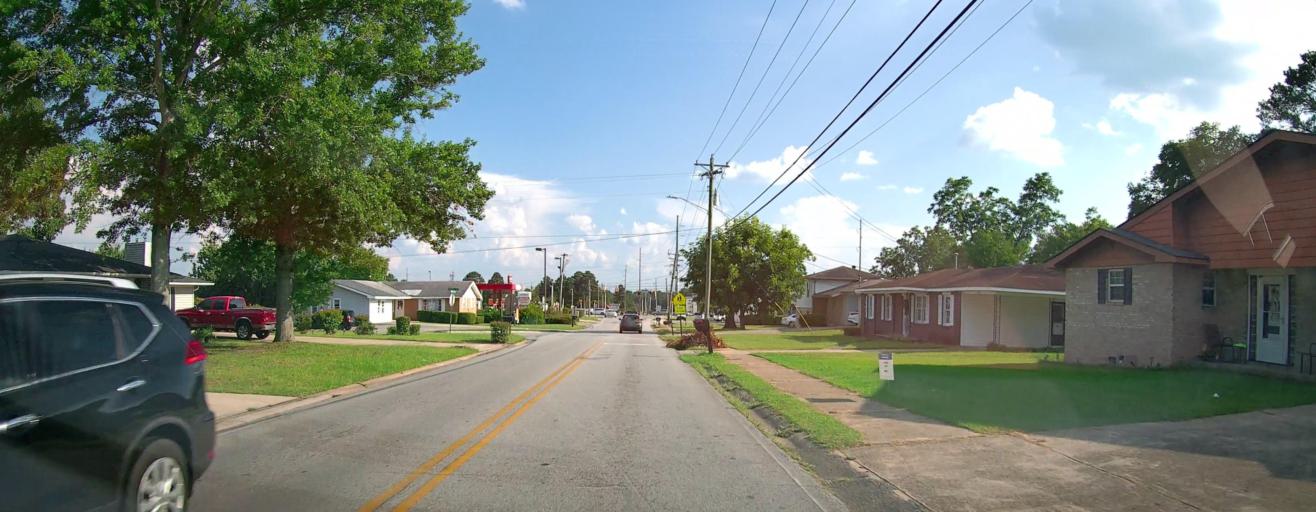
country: US
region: Georgia
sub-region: Houston County
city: Warner Robins
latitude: 32.5955
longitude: -83.6369
